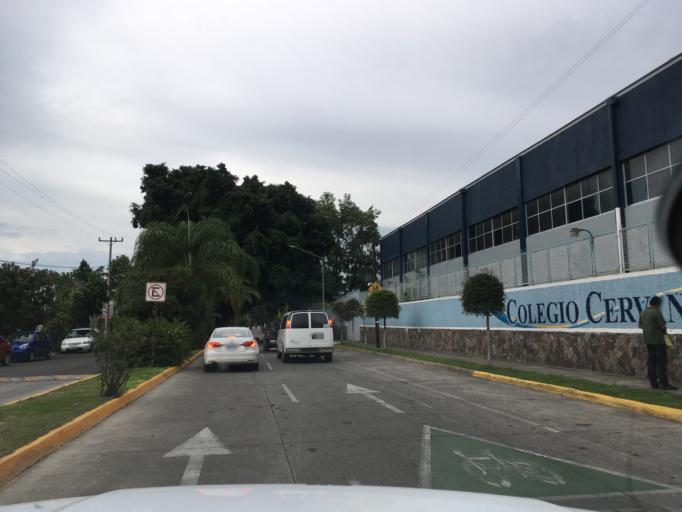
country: MX
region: Jalisco
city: Guadalajara
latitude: 20.6576
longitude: -103.3931
